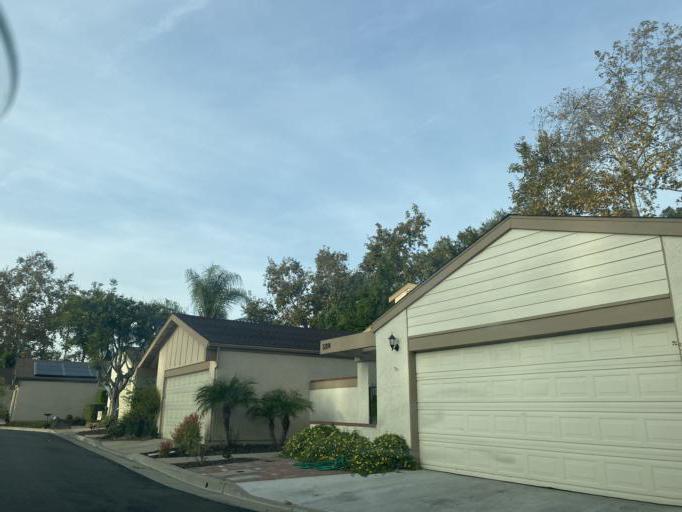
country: US
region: California
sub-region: Orange County
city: Brea
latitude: 33.9091
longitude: -117.8784
